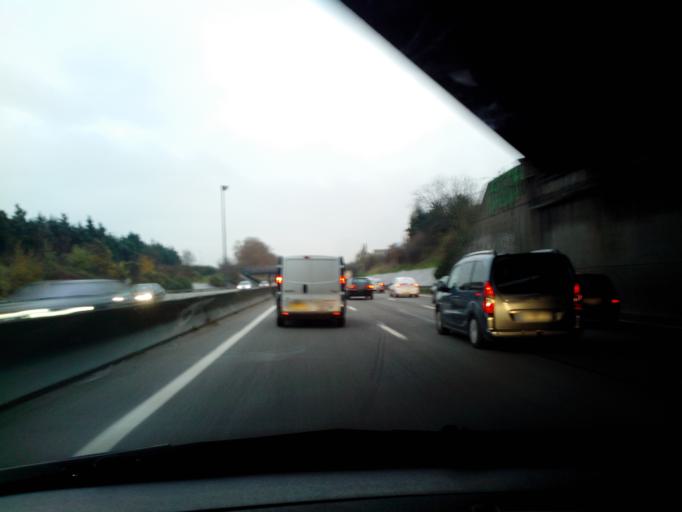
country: FR
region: Ile-de-France
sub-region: Departement de l'Essonne
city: Wissous
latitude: 48.7357
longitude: 2.3167
